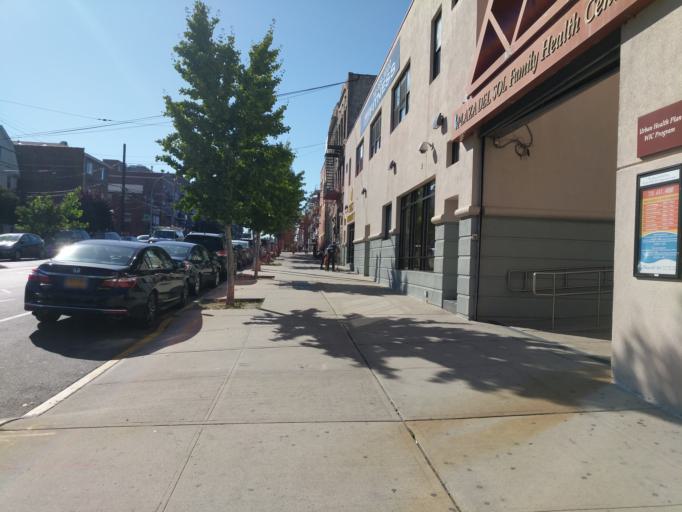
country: US
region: New York
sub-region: Queens County
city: Borough of Queens
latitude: 40.7537
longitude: -73.8605
